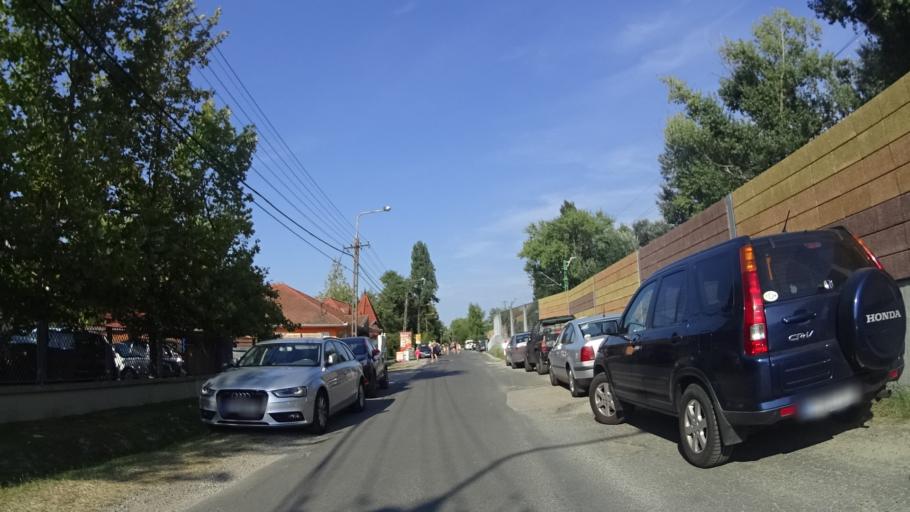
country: HU
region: Somogy
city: Balatonszarszo
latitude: 46.8381
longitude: 17.8460
